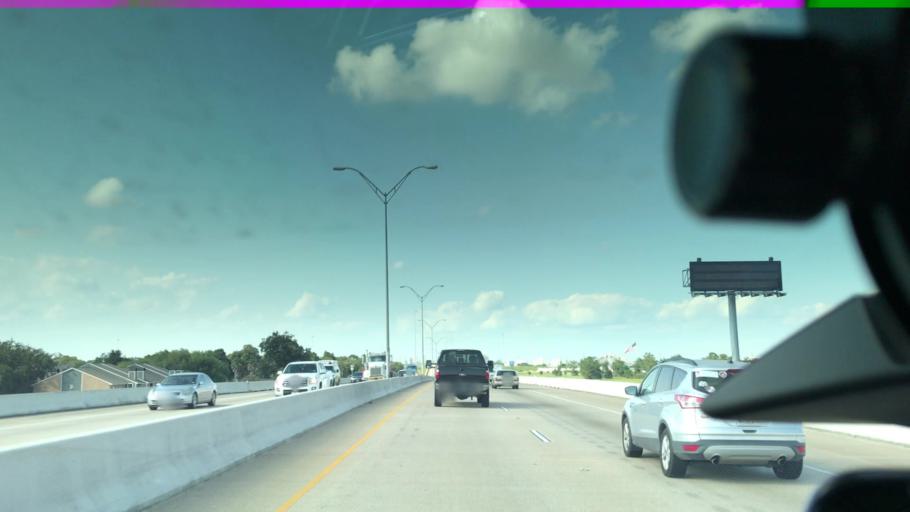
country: US
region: Texas
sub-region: Harris County
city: Deer Park
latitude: 29.7016
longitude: -95.1535
